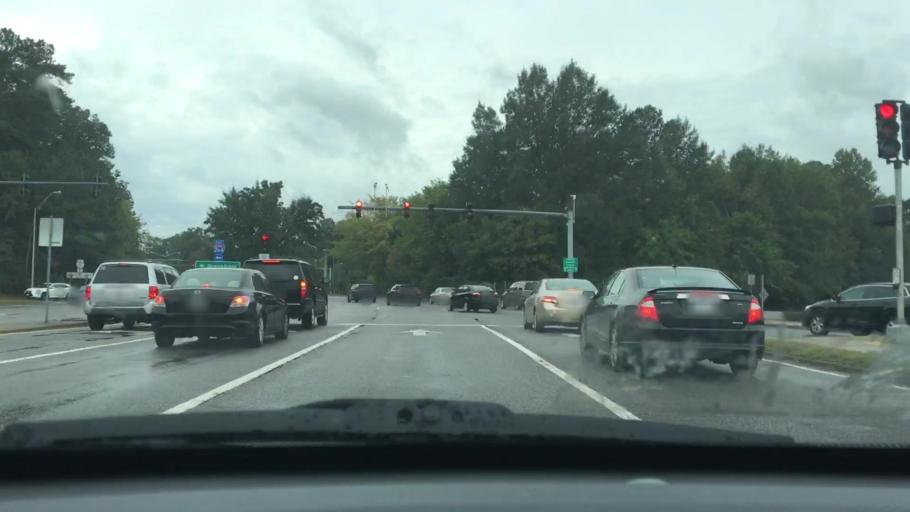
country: US
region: Virginia
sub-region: City of Virginia Beach
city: Virginia Beach
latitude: 36.8352
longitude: -76.0669
